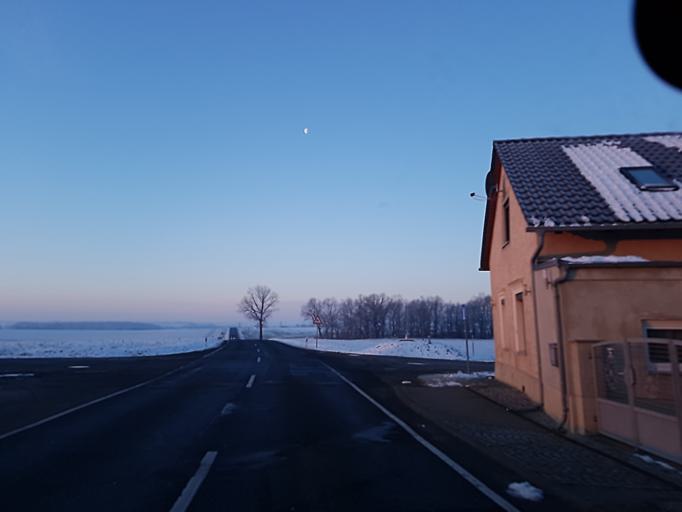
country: DE
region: Saxony
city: Oschatz
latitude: 51.2808
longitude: 13.1300
